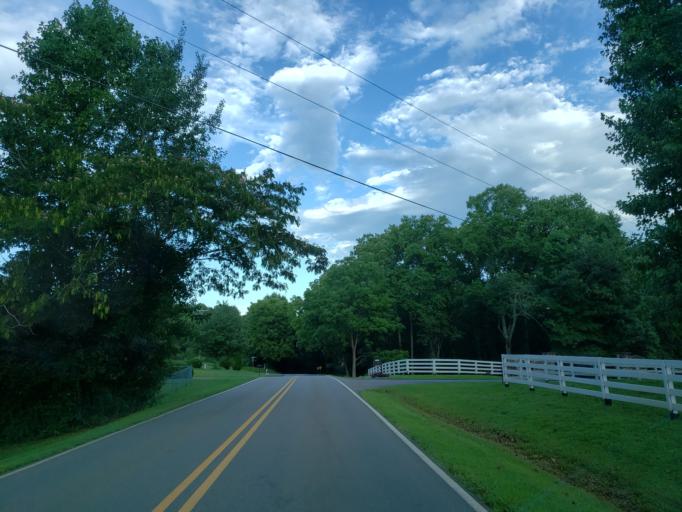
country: US
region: Georgia
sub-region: Cherokee County
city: Ball Ground
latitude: 34.3359
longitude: -84.4436
